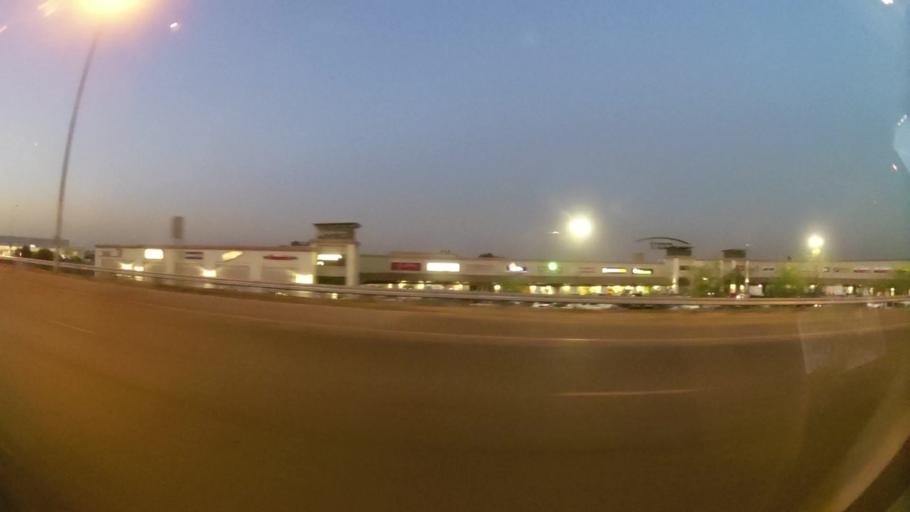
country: ZA
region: North-West
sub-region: Bojanala Platinum District Municipality
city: Rustenburg
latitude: -25.6955
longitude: 27.2537
